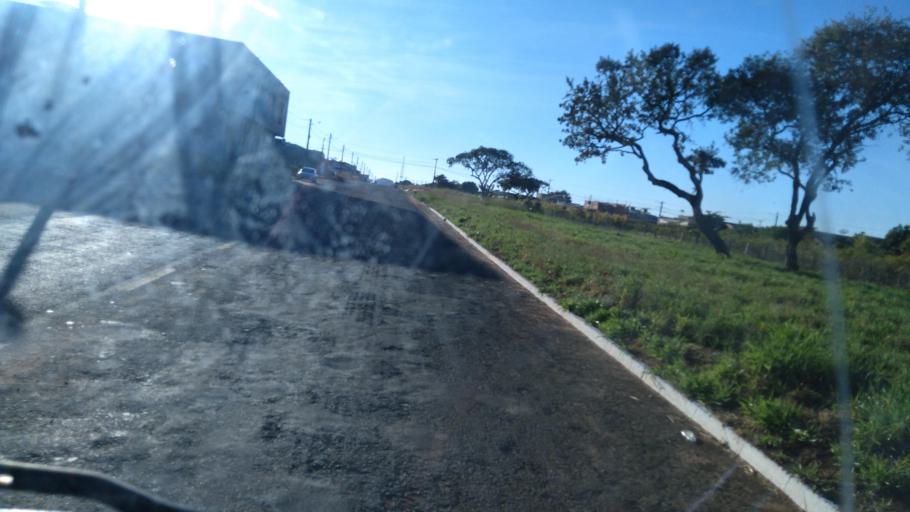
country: BR
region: Goias
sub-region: Mineiros
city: Mineiros
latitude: -17.5468
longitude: -52.5557
